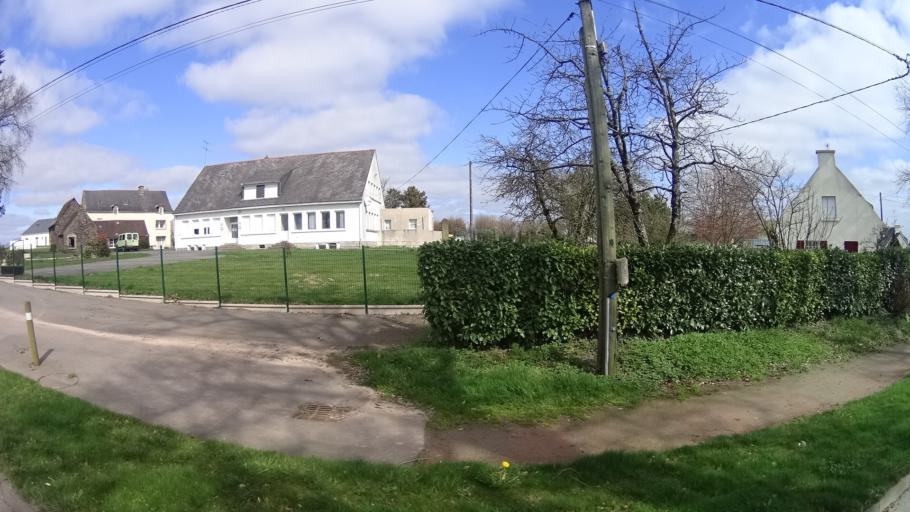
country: FR
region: Brittany
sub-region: Departement du Morbihan
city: Ruffiac
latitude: 47.8224
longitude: -2.2870
